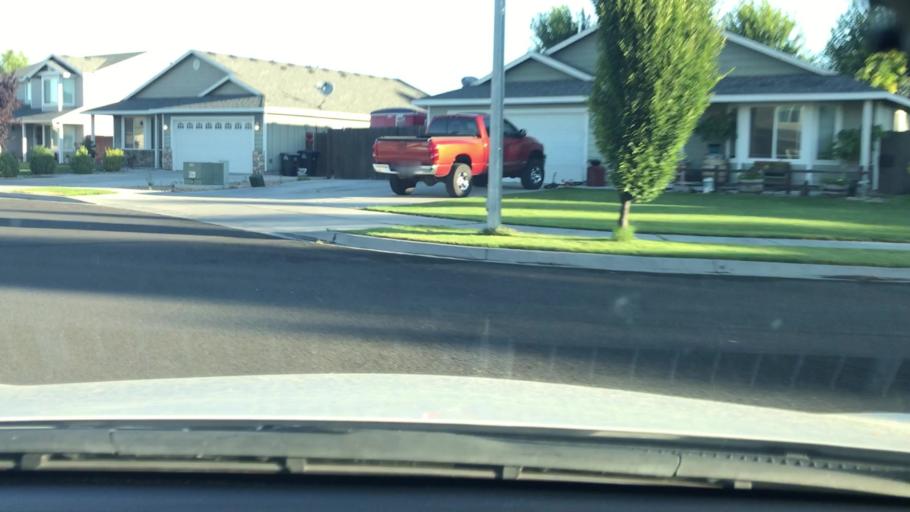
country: US
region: Washington
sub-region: Grant County
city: Moses Lake
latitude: 47.1206
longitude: -119.2524
